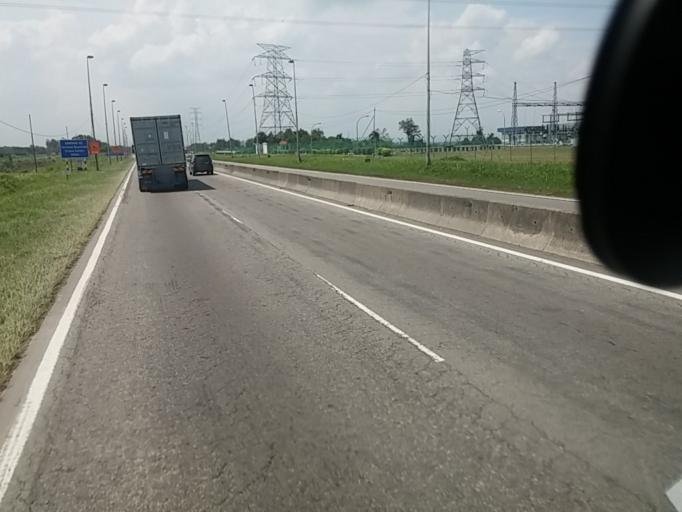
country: MY
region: Selangor
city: Klang
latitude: 2.9667
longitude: 101.3609
